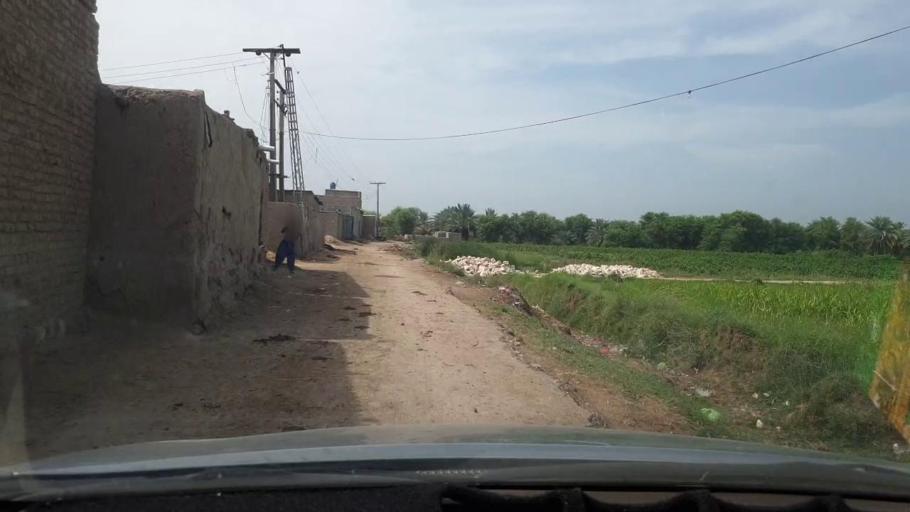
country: PK
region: Sindh
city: Khairpur
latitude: 27.4995
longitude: 68.7548
